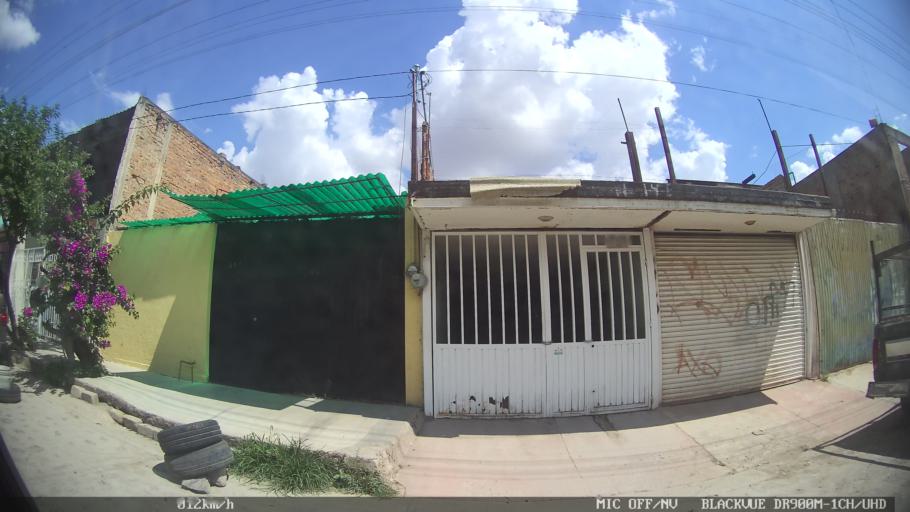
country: MX
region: Jalisco
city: Tlaquepaque
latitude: 20.6713
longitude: -103.2587
